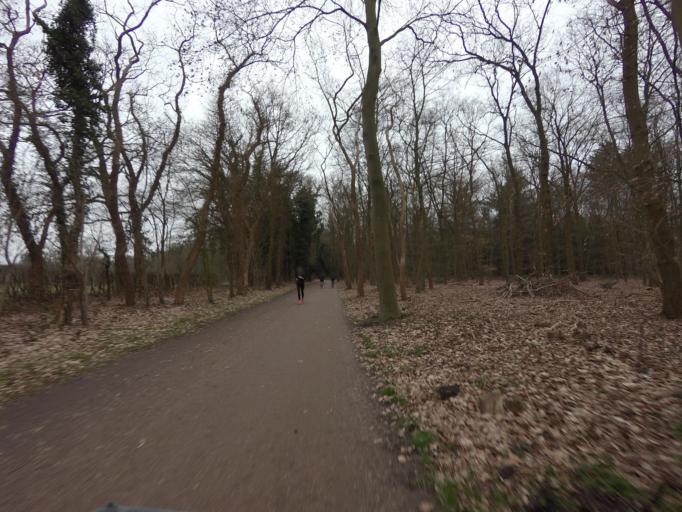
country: NL
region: North Holland
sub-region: Gemeente Hilversum
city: Hilversum
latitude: 52.2289
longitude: 5.1504
